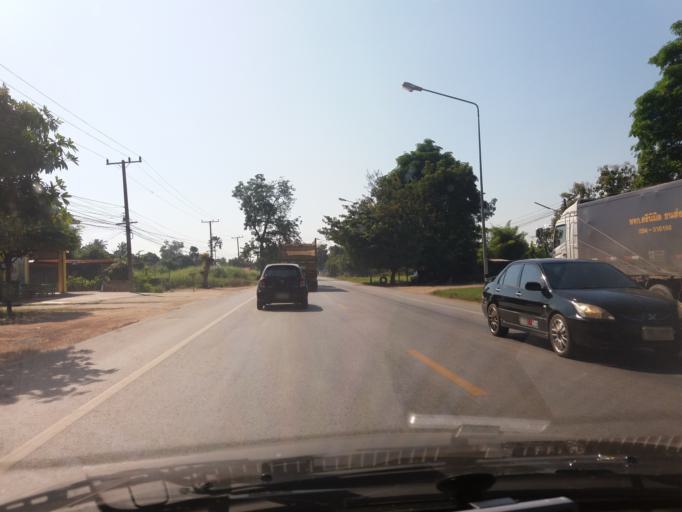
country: TH
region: Kamphaeng Phet
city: Khlong Khlung
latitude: 16.1653
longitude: 99.8016
